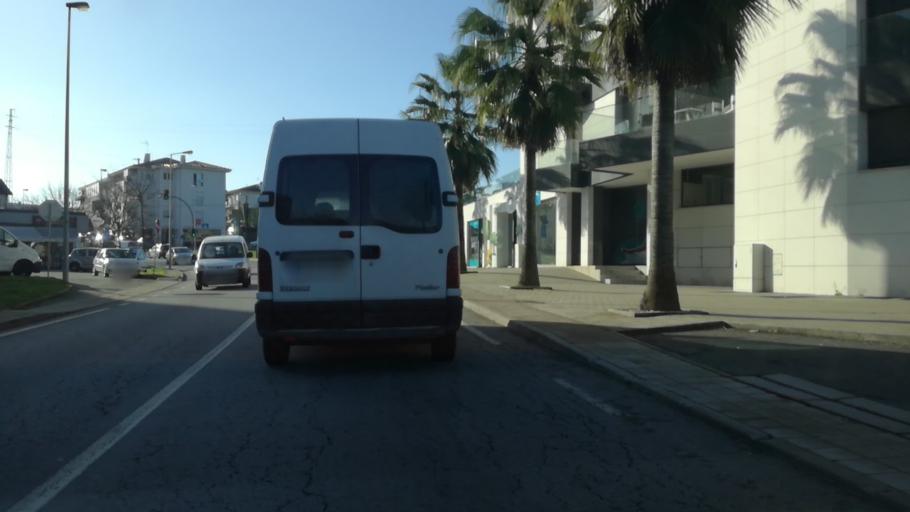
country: PT
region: Braga
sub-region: Guimaraes
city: Ponte
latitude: 41.4881
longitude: -8.3497
